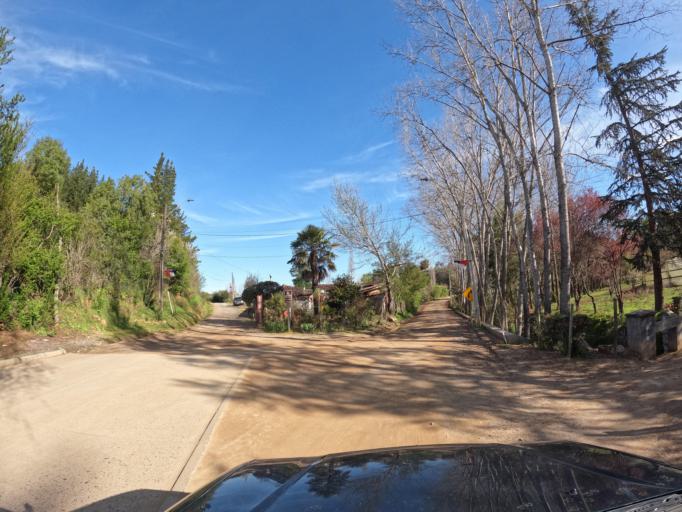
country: CL
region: Biobio
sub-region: Provincia de Biobio
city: La Laja
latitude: -37.1368
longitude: -72.7259
